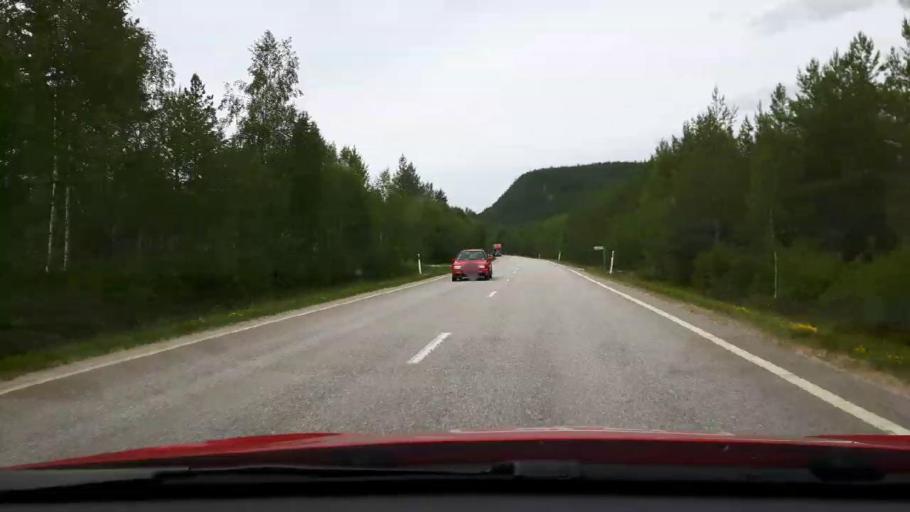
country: SE
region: Jaemtland
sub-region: Harjedalens Kommun
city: Sveg
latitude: 62.0946
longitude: 14.2376
